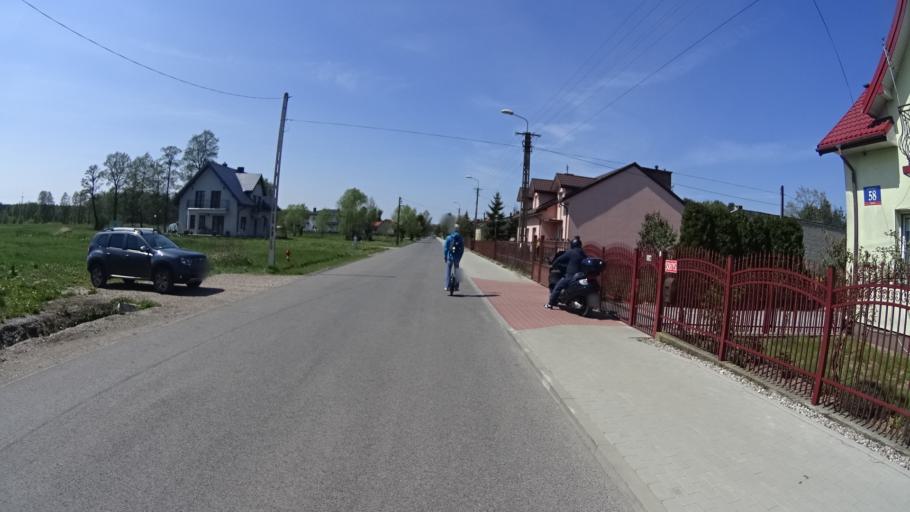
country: PL
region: Masovian Voivodeship
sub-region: Powiat warszawski zachodni
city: Truskaw
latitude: 52.2831
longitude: 20.7374
